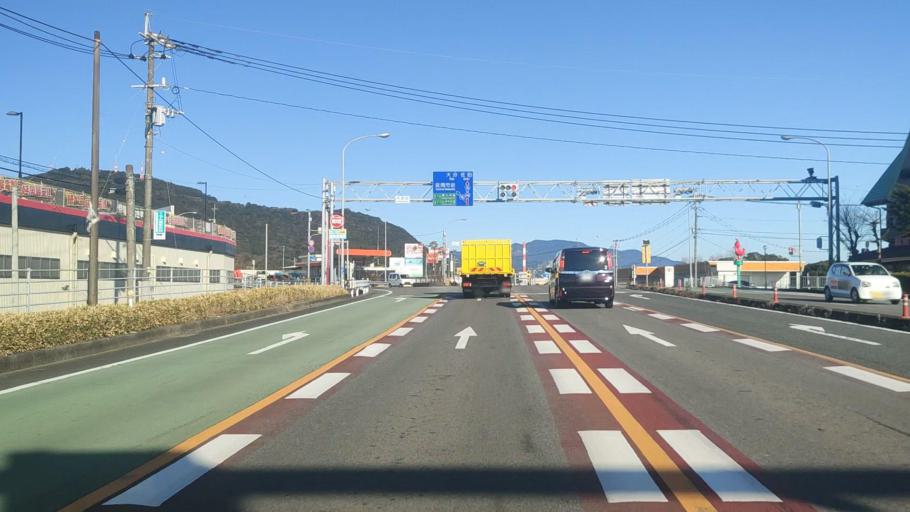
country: JP
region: Miyazaki
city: Nobeoka
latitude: 32.5444
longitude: 131.6780
